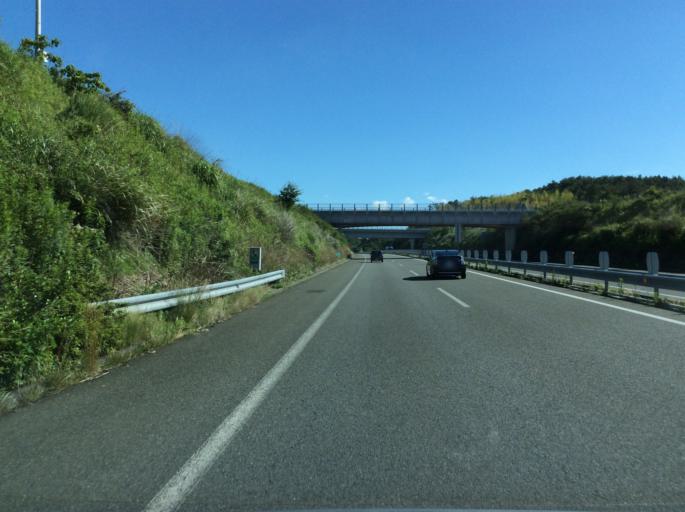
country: JP
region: Fukushima
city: Namie
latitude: 37.3042
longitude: 140.9902
